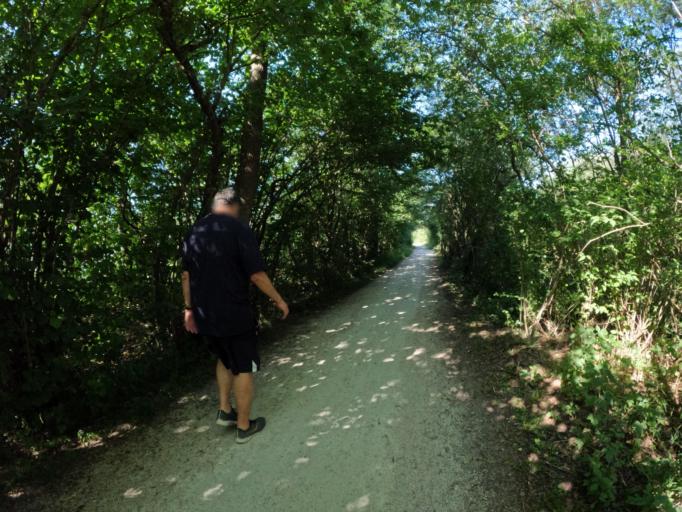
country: DE
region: Bavaria
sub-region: Upper Bavaria
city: Ubersee
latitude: 47.8575
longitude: 12.4764
